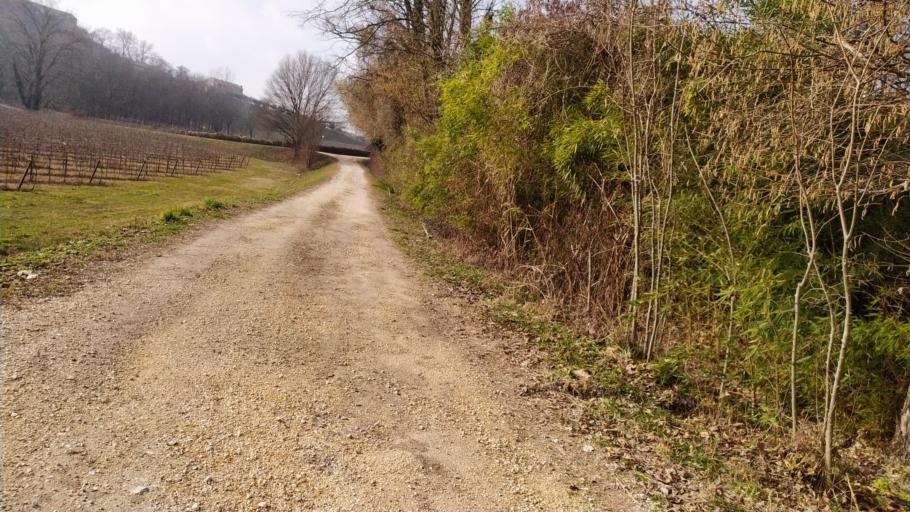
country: IT
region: Veneto
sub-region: Provincia di Treviso
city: Colle Umberto
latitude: 45.9254
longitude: 12.3417
